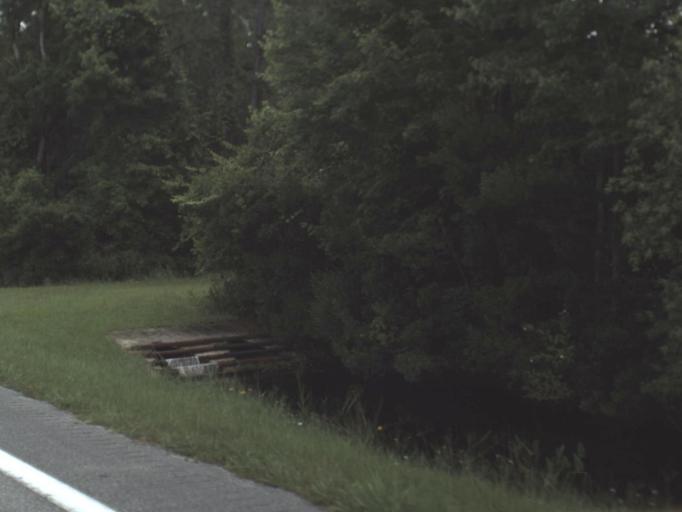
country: US
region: Florida
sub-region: Levy County
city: Bronson
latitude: 29.3948
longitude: -82.6985
